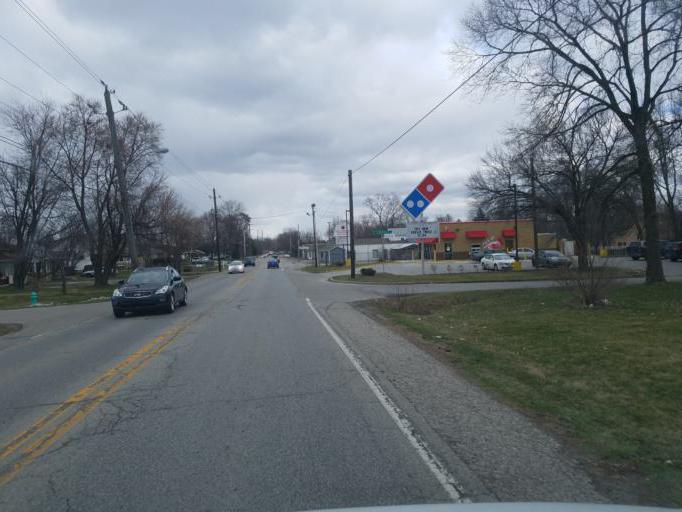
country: US
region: Indiana
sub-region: Marion County
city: Speedway
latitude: 39.7645
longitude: -86.2394
